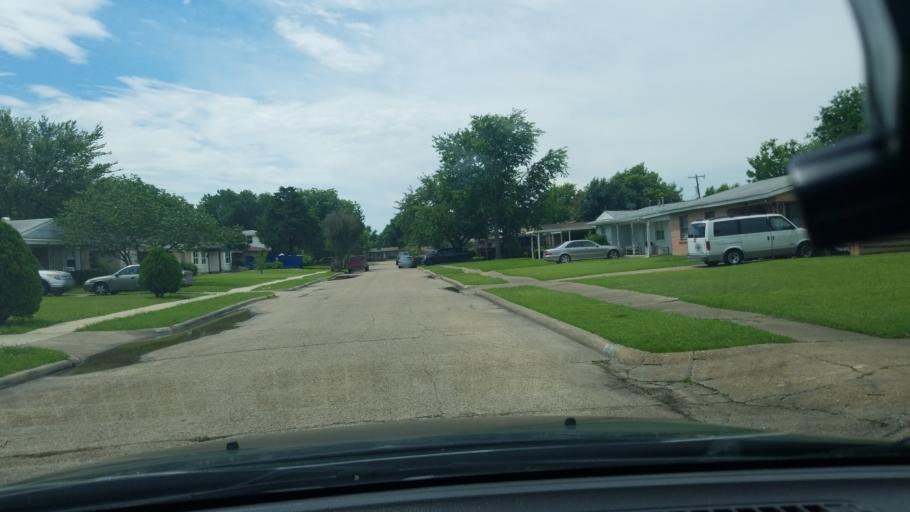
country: US
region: Texas
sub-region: Dallas County
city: Mesquite
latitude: 32.7555
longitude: -96.5818
